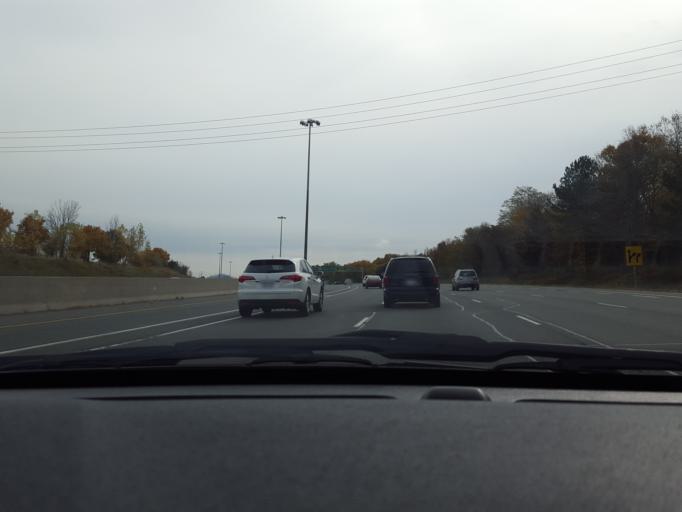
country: CA
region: Ontario
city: Willowdale
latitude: 43.8186
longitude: -79.3602
